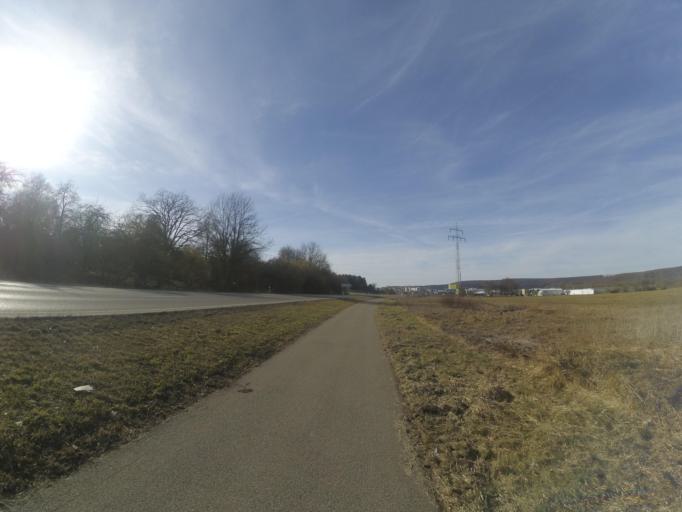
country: DE
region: Baden-Wuerttemberg
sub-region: Regierungsbezirk Stuttgart
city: Giengen an der Brenz
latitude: 48.6240
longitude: 10.2108
